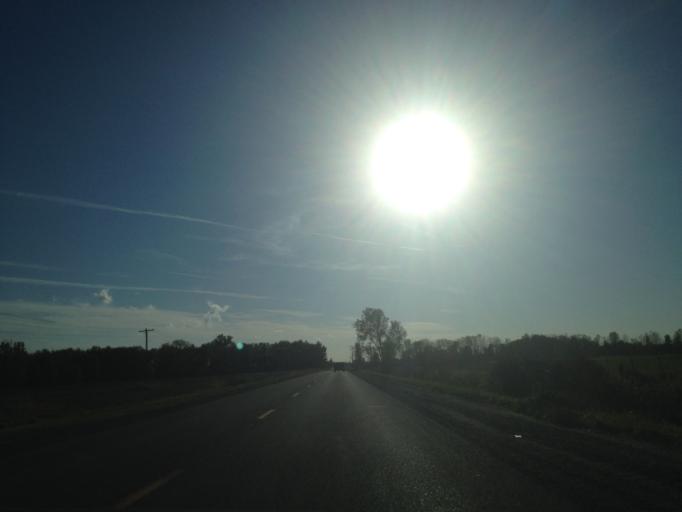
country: CA
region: Ontario
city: Delaware
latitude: 42.6418
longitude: -81.5540
